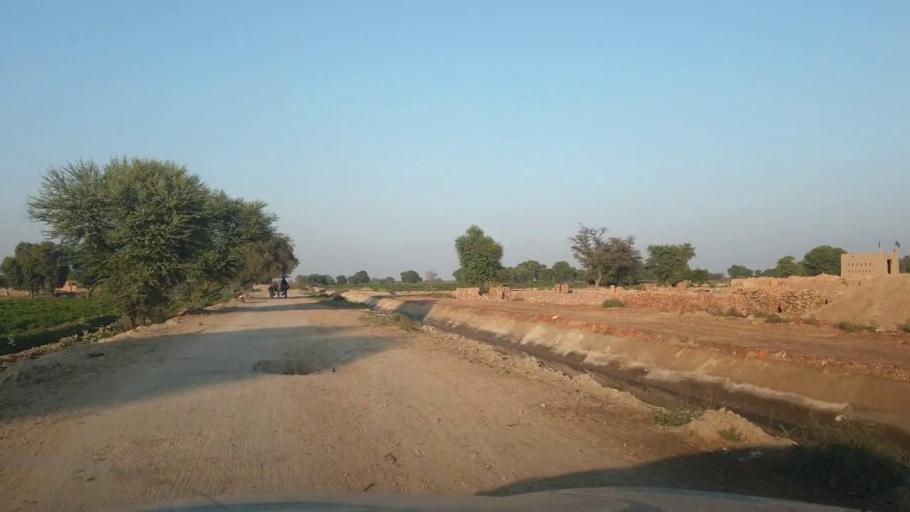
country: PK
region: Sindh
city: Bhan
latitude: 26.5493
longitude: 67.7388
